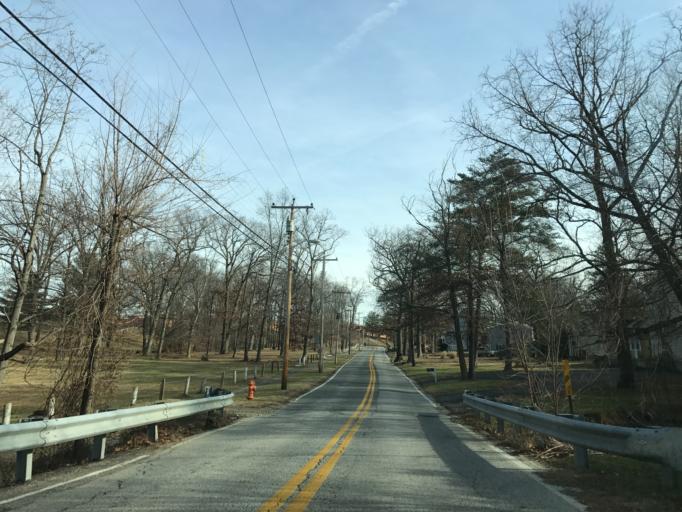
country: US
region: Maryland
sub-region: Baltimore County
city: Carney
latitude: 39.4057
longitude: -76.5322
